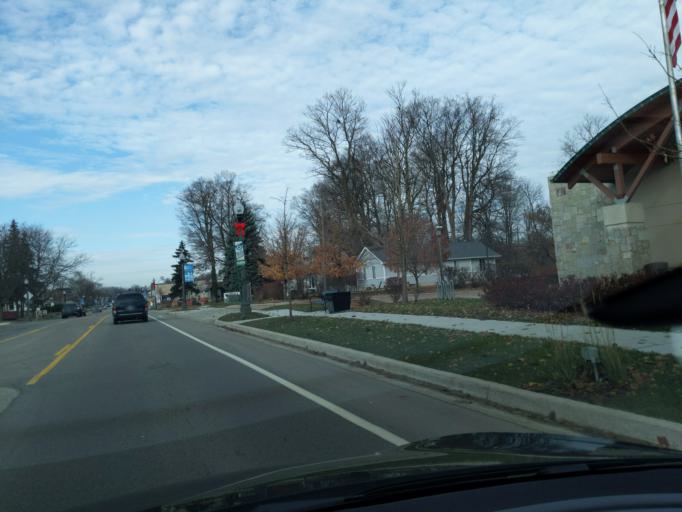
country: US
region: Michigan
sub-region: Ingham County
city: Holt
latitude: 42.6435
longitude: -84.5187
